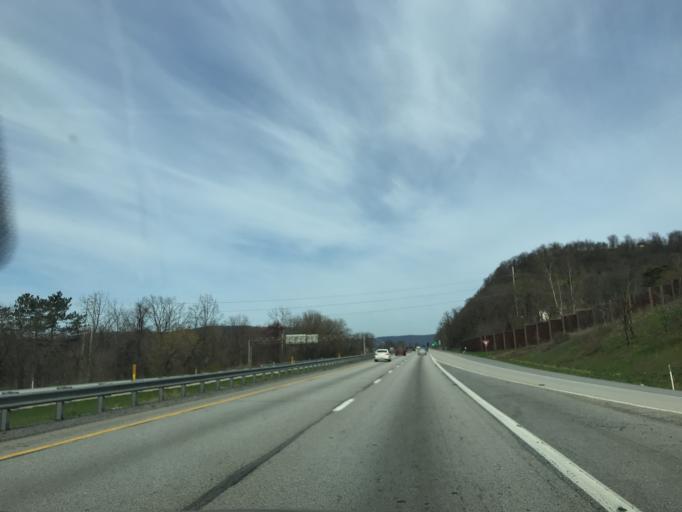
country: US
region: Pennsylvania
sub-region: Perry County
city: Marysville
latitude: 40.3281
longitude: -76.8933
